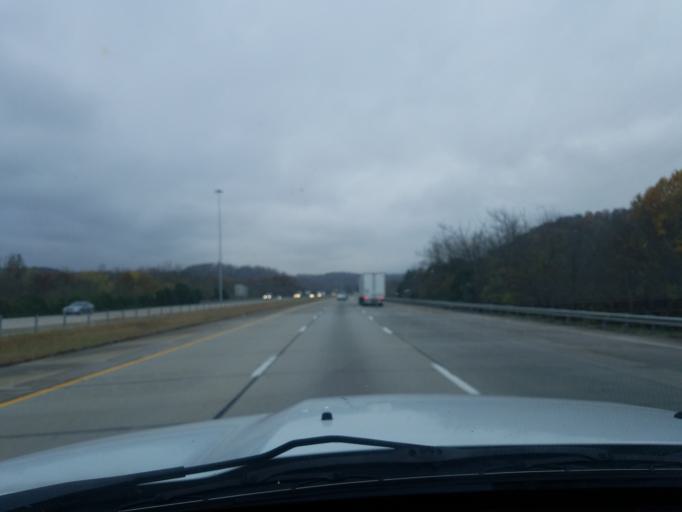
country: US
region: Kentucky
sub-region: Bullitt County
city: Lebanon Junction
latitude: 37.7989
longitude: -85.7513
